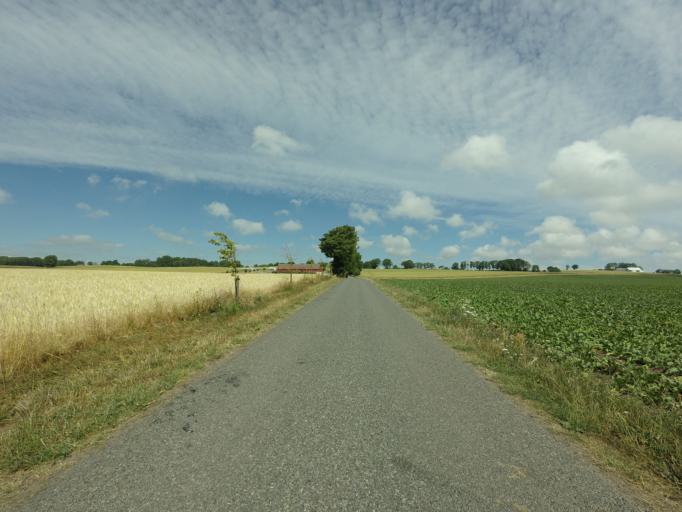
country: SE
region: Skane
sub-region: Simrishamns Kommun
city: Simrishamn
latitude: 55.4890
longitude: 14.3106
